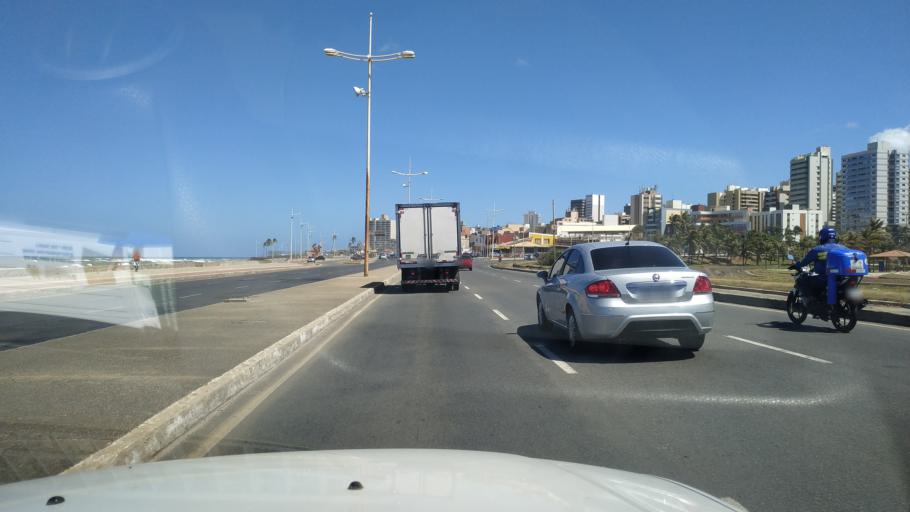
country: BR
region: Bahia
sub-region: Salvador
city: Salvador
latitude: -12.9987
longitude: -38.4469
